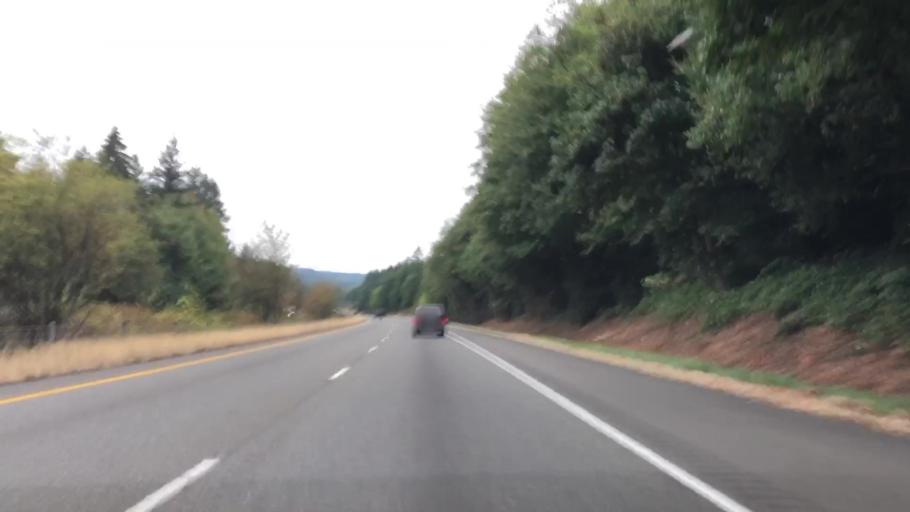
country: US
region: Washington
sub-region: Pierce County
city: Purdy
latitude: 47.3922
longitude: -122.6175
